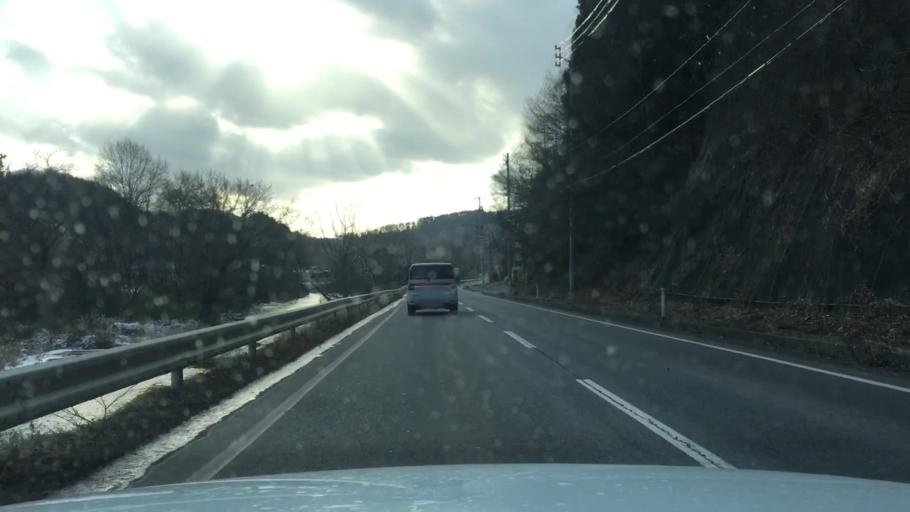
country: JP
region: Iwate
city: Morioka-shi
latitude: 39.6765
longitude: 141.2200
